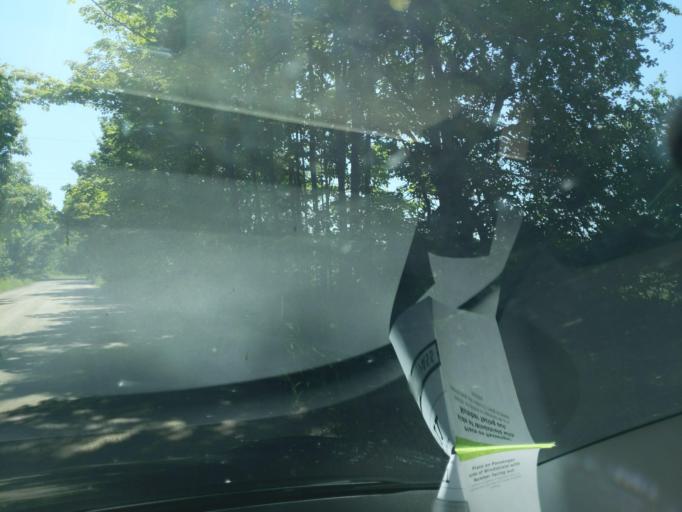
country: US
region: Michigan
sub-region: Cheboygan County
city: Cheboygan
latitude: 45.6536
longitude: -84.6322
